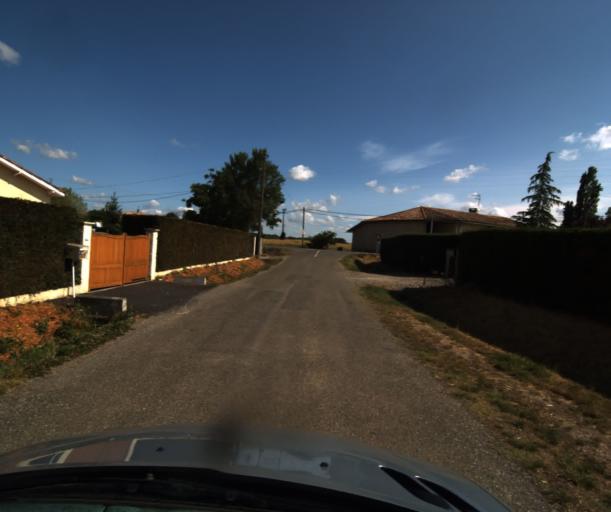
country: FR
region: Midi-Pyrenees
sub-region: Departement du Tarn-et-Garonne
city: Finhan
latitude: 43.9161
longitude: 1.2713
